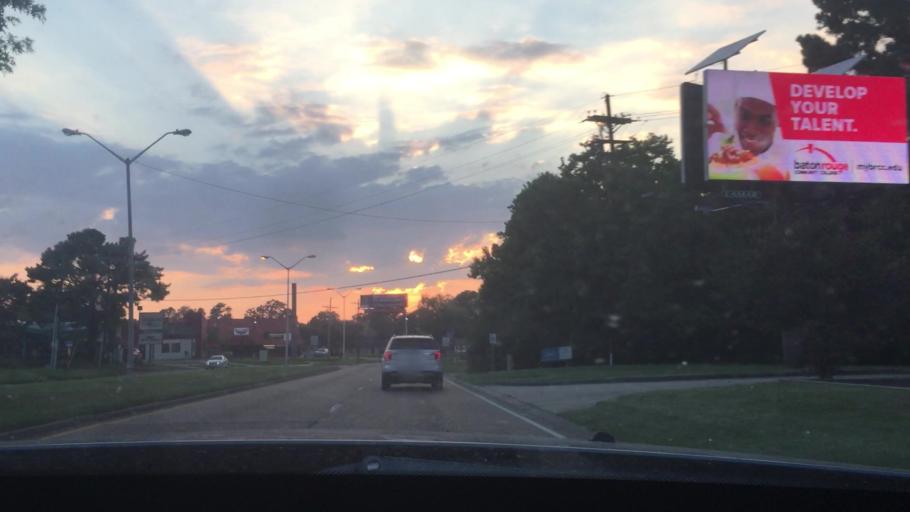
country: US
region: Louisiana
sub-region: East Baton Rouge Parish
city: Westminster
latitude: 30.4265
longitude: -91.0538
